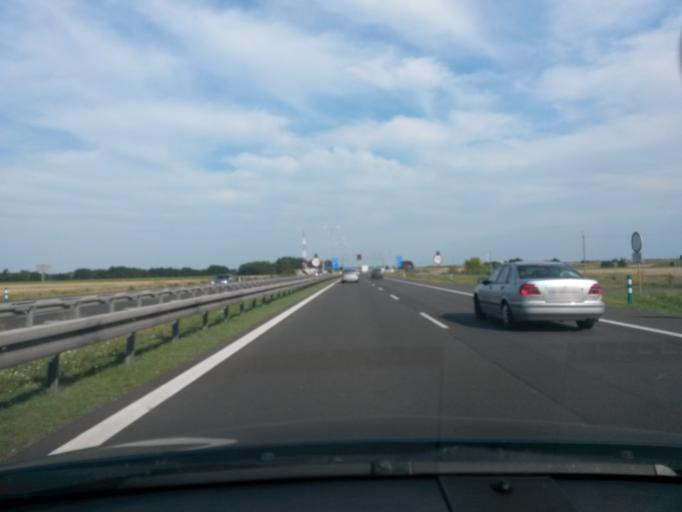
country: PL
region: Greater Poland Voivodeship
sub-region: Powiat slupecki
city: Ladek
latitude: 52.2241
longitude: 17.9429
